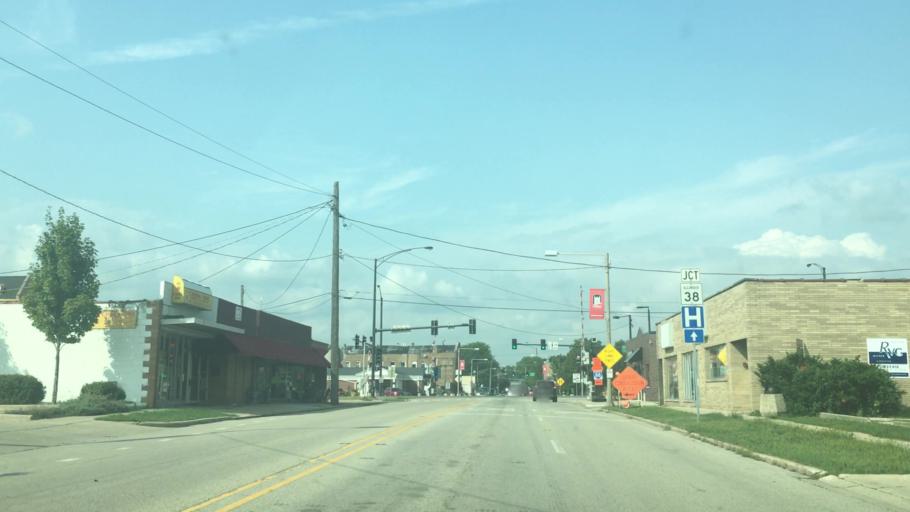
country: US
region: Illinois
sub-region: DeKalb County
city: DeKalb
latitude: 41.9287
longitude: -88.7504
